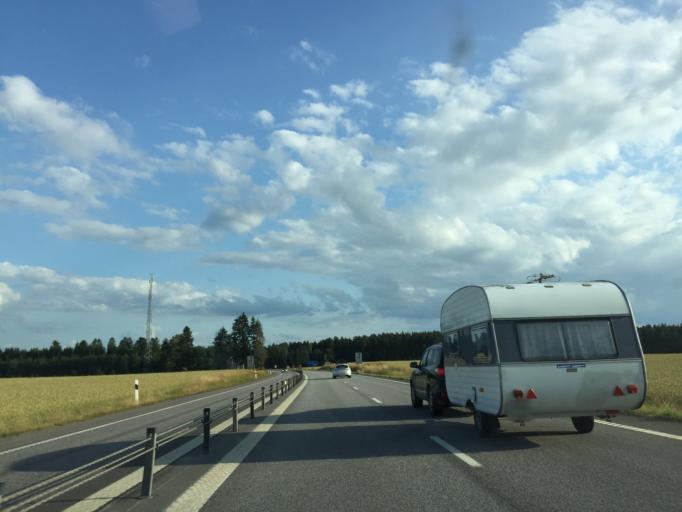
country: SE
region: OEstergoetland
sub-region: Motala Kommun
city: Motala
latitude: 58.5816
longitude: 14.9862
